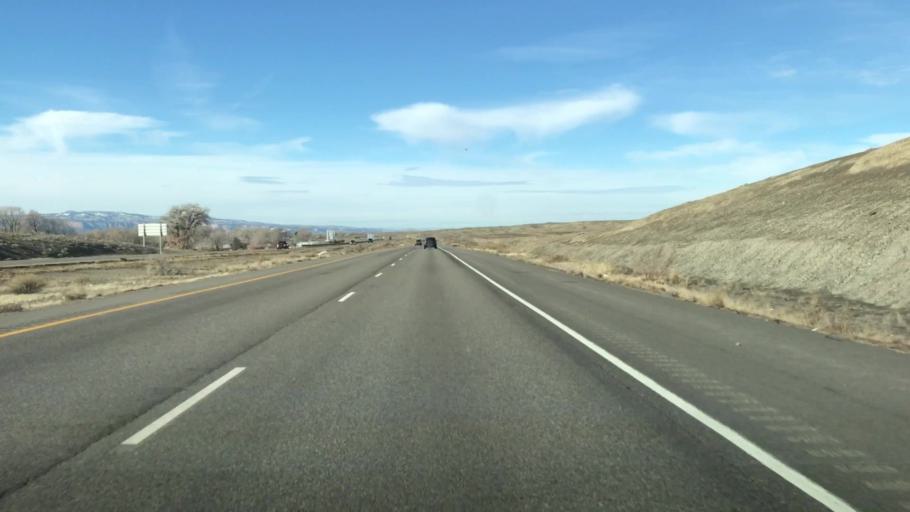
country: US
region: Colorado
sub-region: Mesa County
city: Clifton
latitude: 39.1034
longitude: -108.4628
